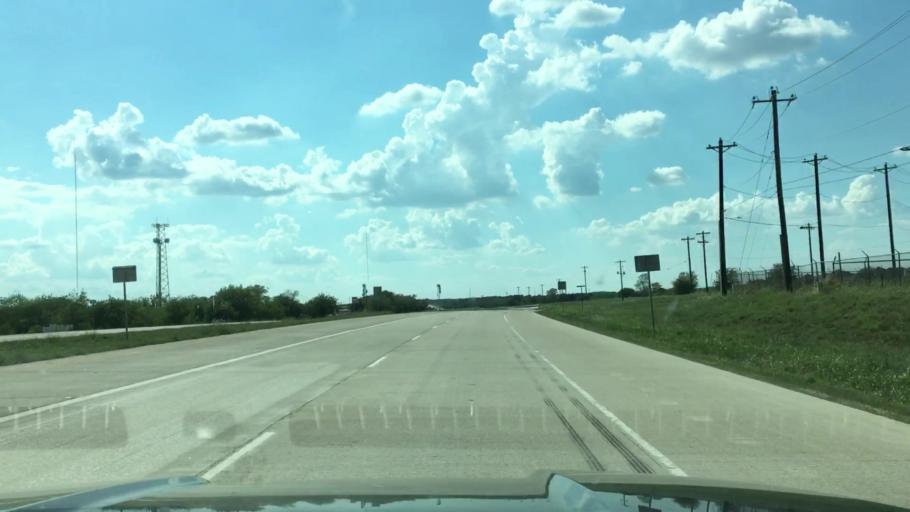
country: US
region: Texas
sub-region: Tarrant County
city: Haslet
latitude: 33.0362
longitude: -97.3904
